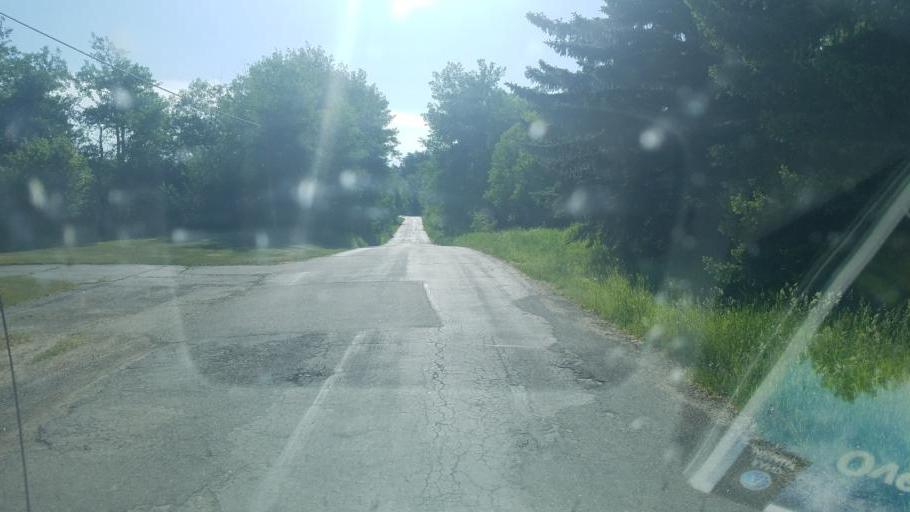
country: US
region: Montana
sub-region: Carbon County
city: Red Lodge
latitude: 45.3601
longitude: -109.1629
